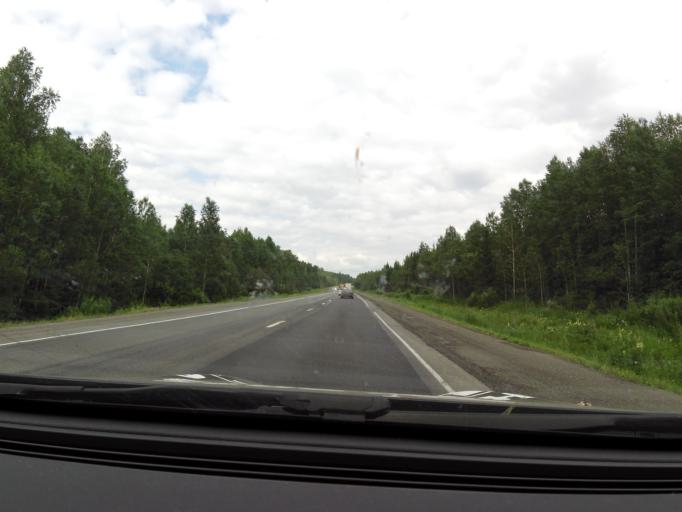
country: RU
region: Sverdlovsk
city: Bilimbay
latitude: 56.8480
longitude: 59.6868
